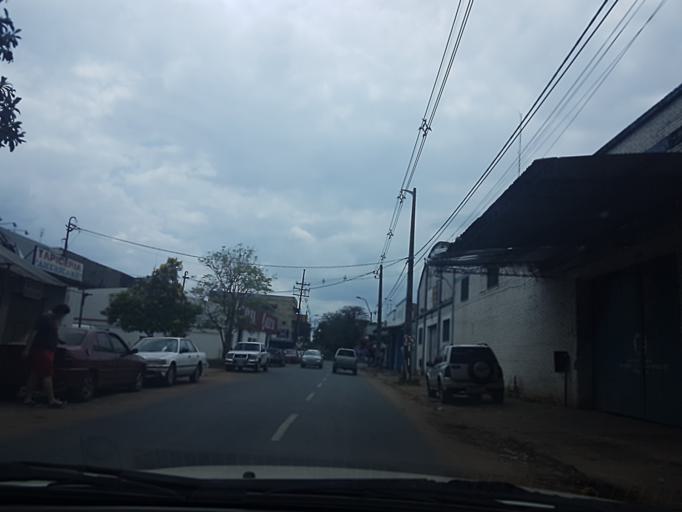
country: PY
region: Asuncion
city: Asuncion
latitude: -25.3064
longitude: -57.6060
